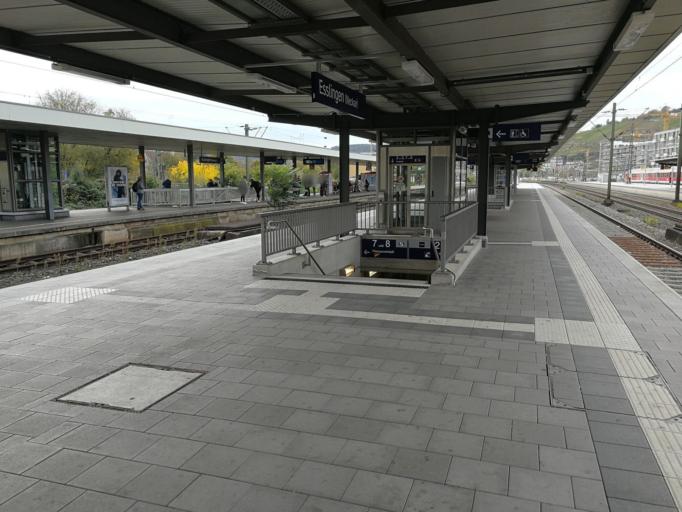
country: DE
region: Baden-Wuerttemberg
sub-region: Regierungsbezirk Stuttgart
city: Esslingen
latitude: 48.7386
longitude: 9.3003
